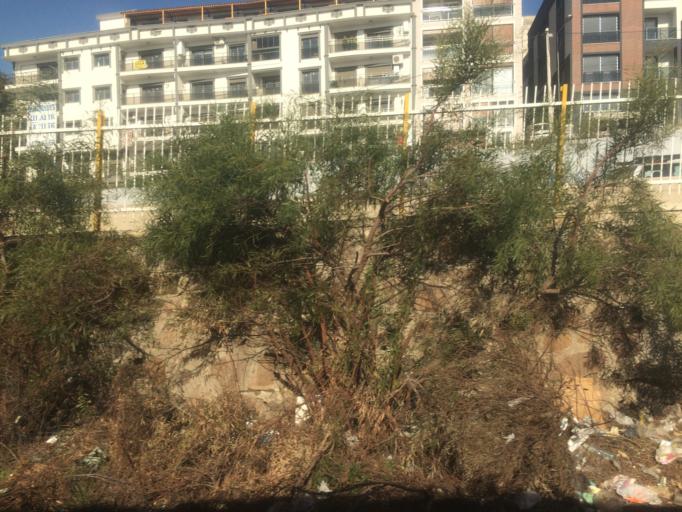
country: TR
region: Izmir
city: Karsiyaka
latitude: 38.4653
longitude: 27.1341
